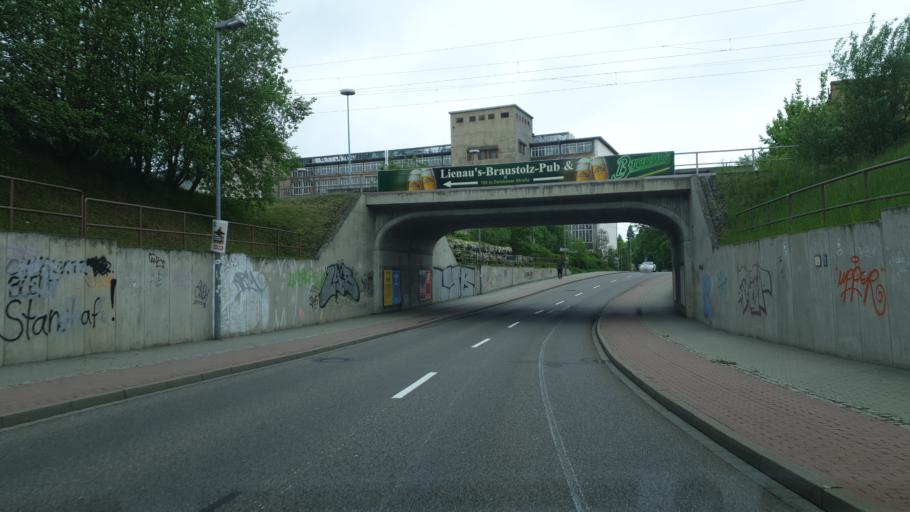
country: DE
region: Saxony
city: Neukirchen
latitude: 50.8187
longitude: 12.8822
